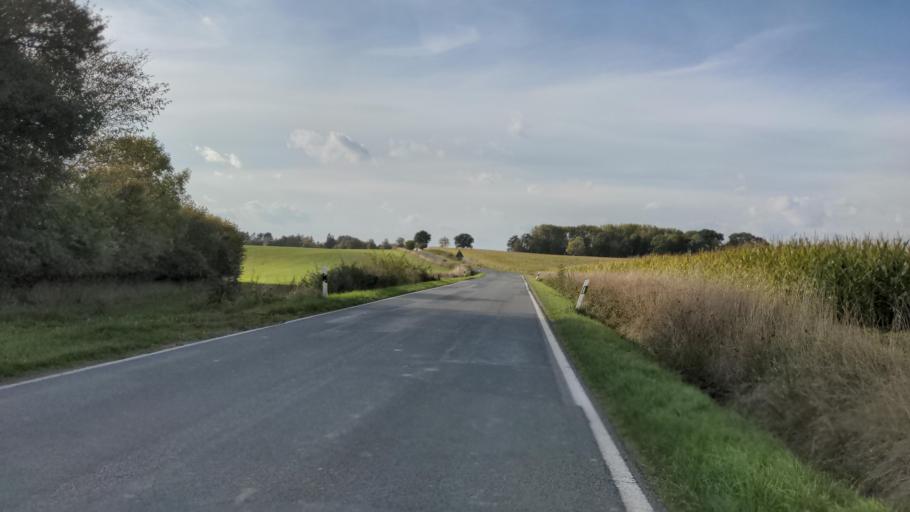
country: DE
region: Schleswig-Holstein
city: Monkhagen
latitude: 53.9550
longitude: 10.5359
